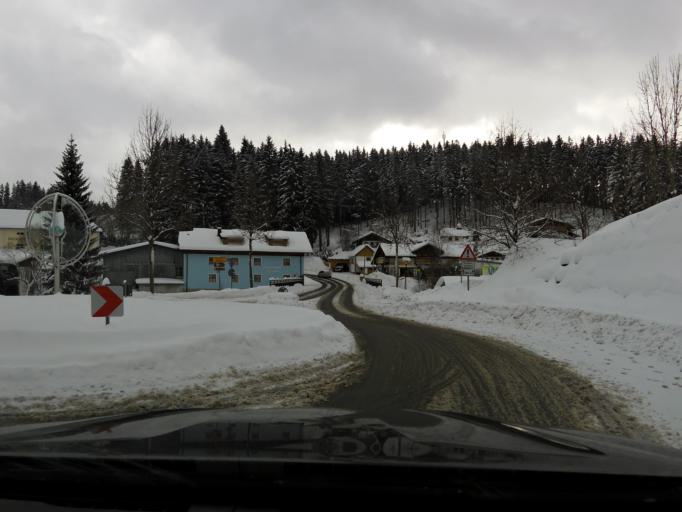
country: DE
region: Bavaria
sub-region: Lower Bavaria
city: Spiegelau
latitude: 48.9126
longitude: 13.3651
